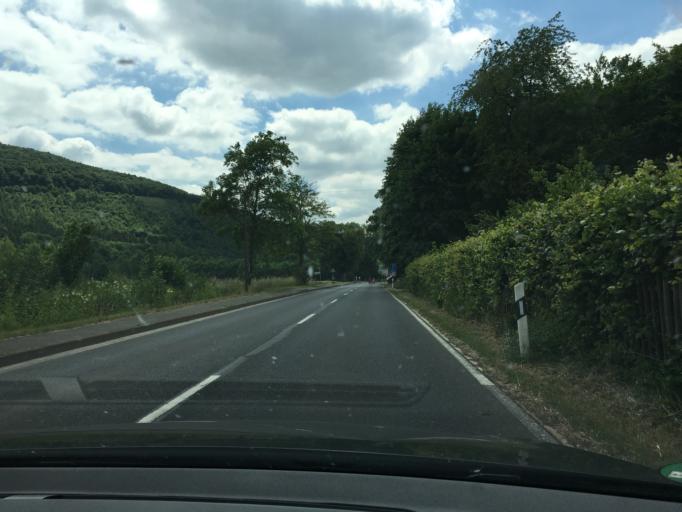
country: DE
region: North Rhine-Westphalia
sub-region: Regierungsbezirk Koln
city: Nideggen
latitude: 50.7211
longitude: 6.4496
